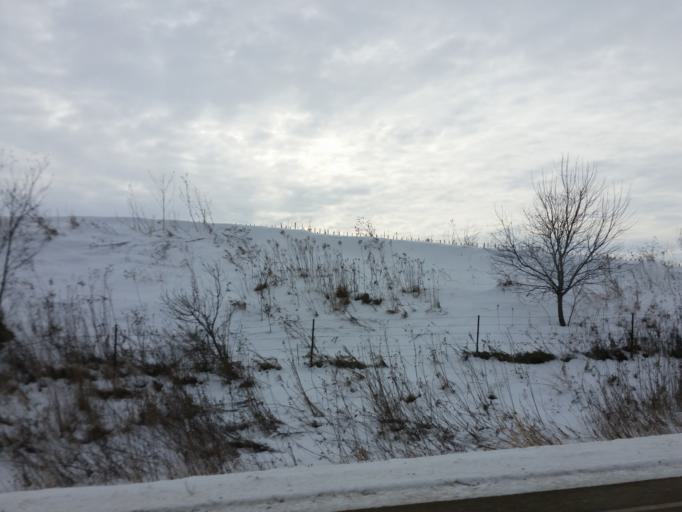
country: US
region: Iowa
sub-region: Dubuque County
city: Asbury
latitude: 42.3821
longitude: -90.7313
